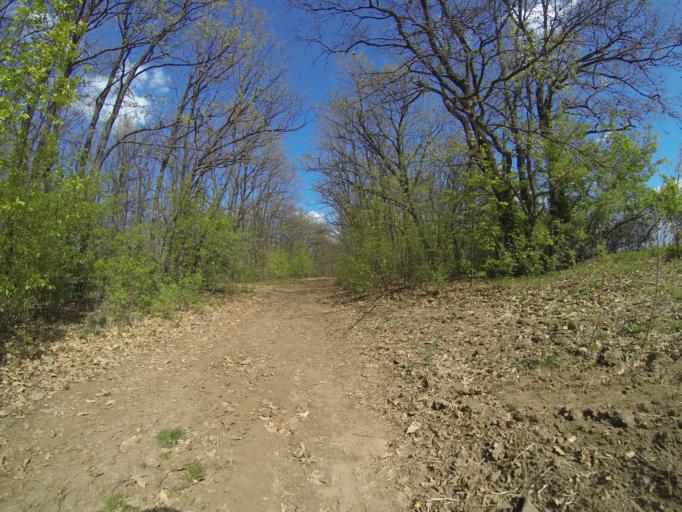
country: RO
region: Dolj
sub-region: Comuna Almaju
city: Almaju
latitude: 44.4901
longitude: 23.7034
